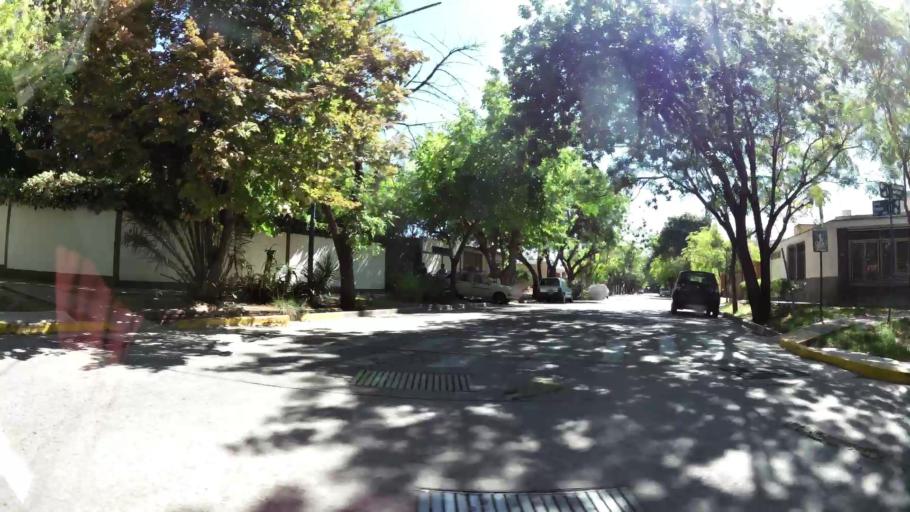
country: AR
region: Mendoza
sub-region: Departamento de Godoy Cruz
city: Godoy Cruz
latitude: -32.9477
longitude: -68.8416
